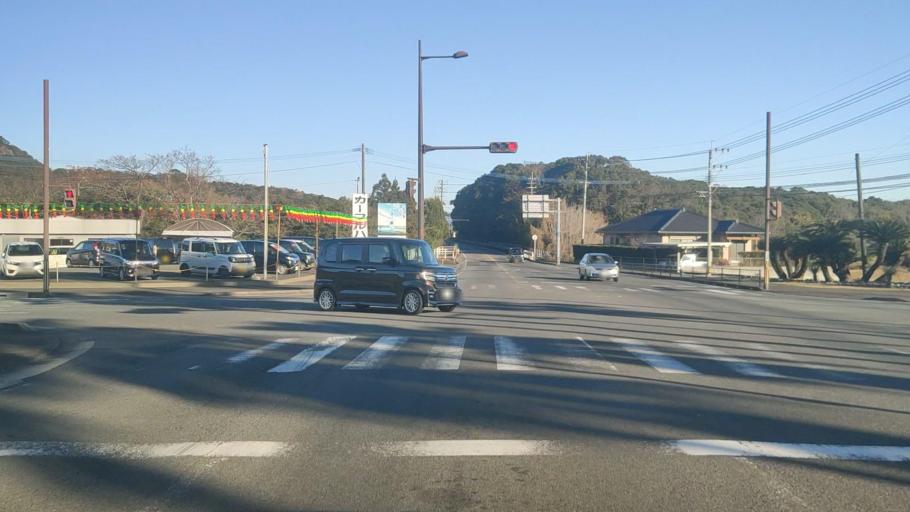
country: JP
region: Miyazaki
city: Nobeoka
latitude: 32.3795
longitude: 131.6276
